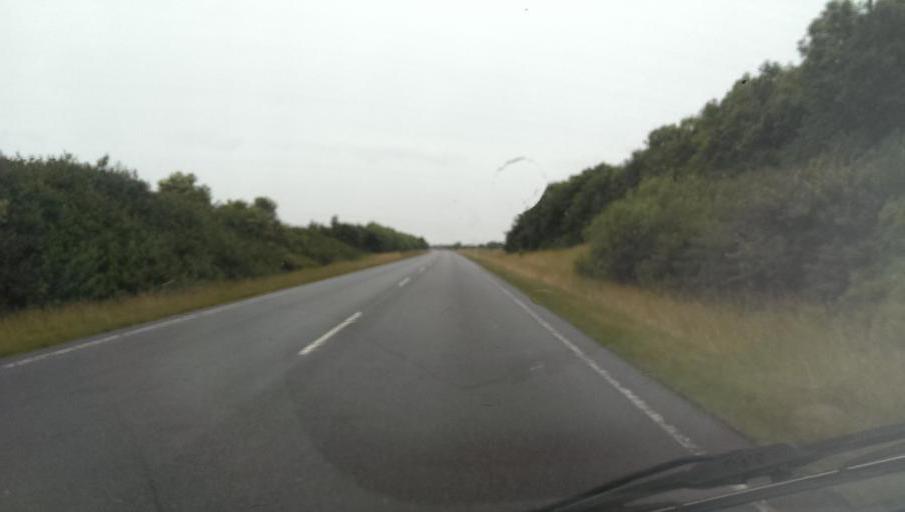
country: DK
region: South Denmark
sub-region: Esbjerg Kommune
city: Esbjerg
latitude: 55.5309
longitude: 8.4307
